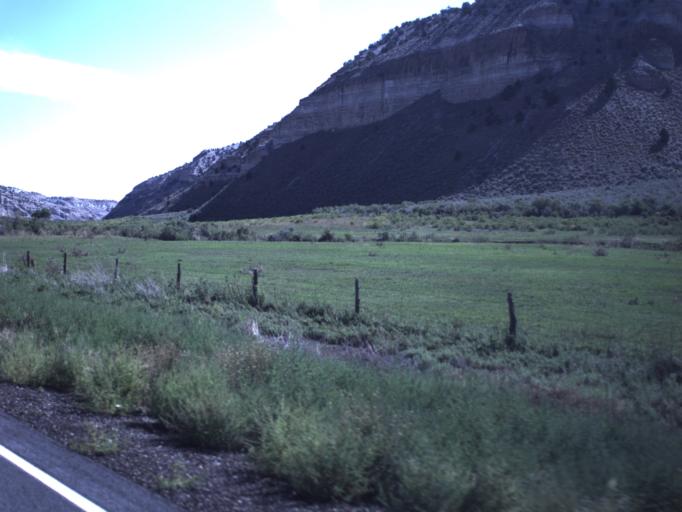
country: US
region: Utah
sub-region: Duchesne County
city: Duchesne
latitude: 40.0841
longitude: -110.4976
